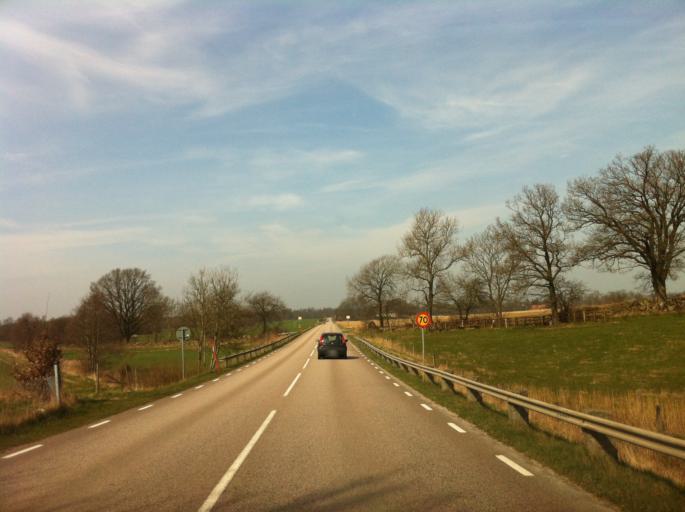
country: SE
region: Skane
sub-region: Svalovs Kommun
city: Svaloev
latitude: 55.9624
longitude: 13.1037
